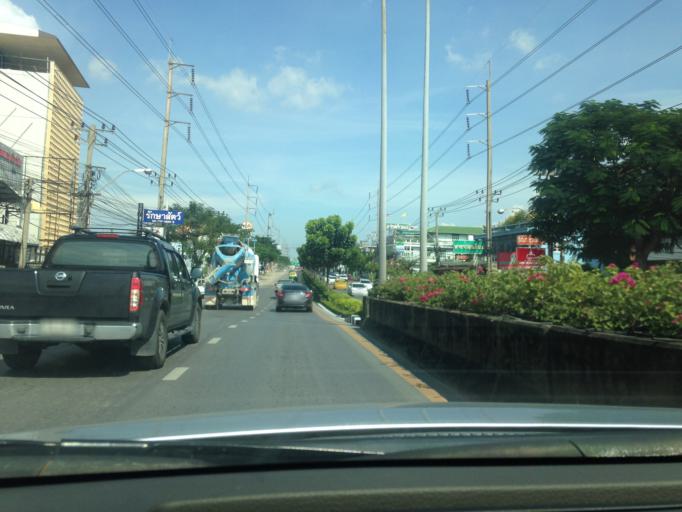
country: TH
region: Bangkok
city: Lat Krabang
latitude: 13.7223
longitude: 100.7296
